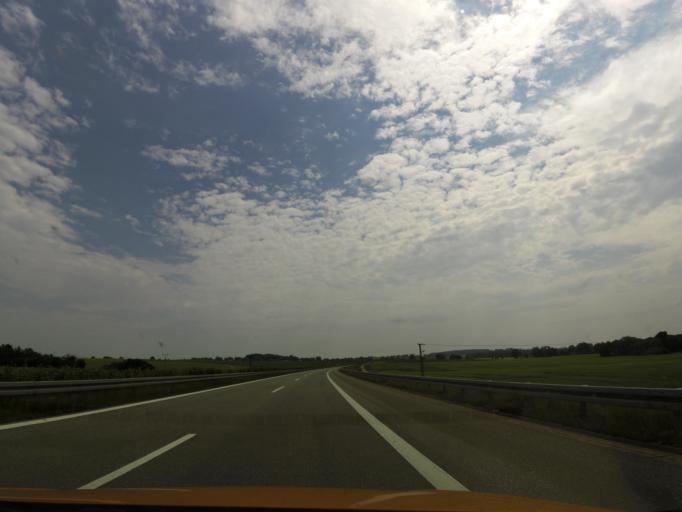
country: DE
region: Mecklenburg-Vorpommern
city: Zurow
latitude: 53.8572
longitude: 11.5901
